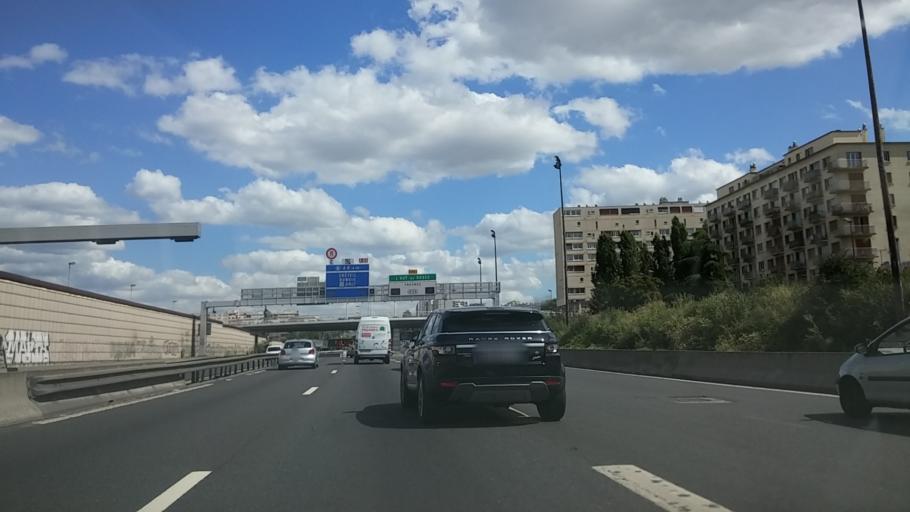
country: FR
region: Ile-de-France
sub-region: Departement du Val-de-Marne
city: Fresnes
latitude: 48.7619
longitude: 2.3145
